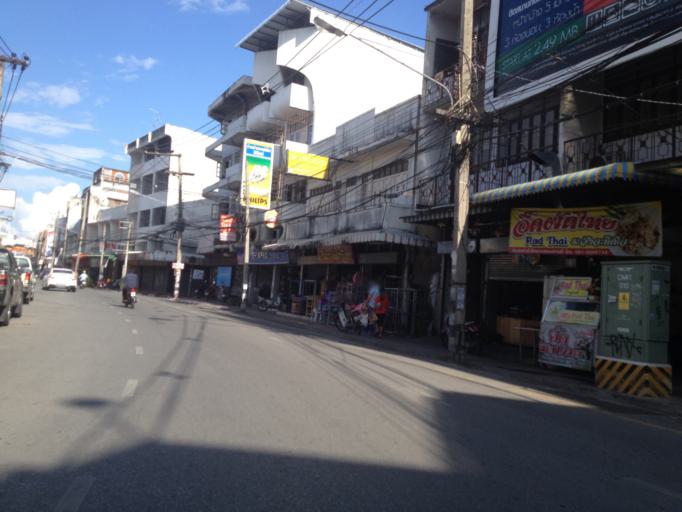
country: TH
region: Chiang Mai
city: Chiang Mai
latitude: 18.7898
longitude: 98.9964
